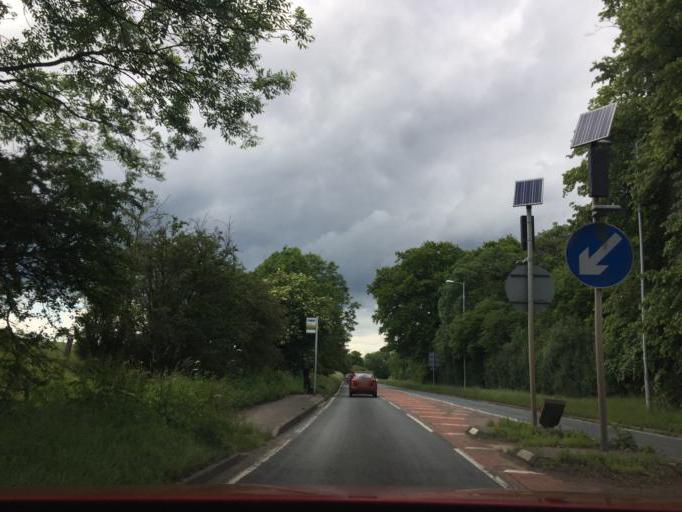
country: GB
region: England
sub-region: Luton
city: Luton
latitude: 51.8470
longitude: -0.4125
